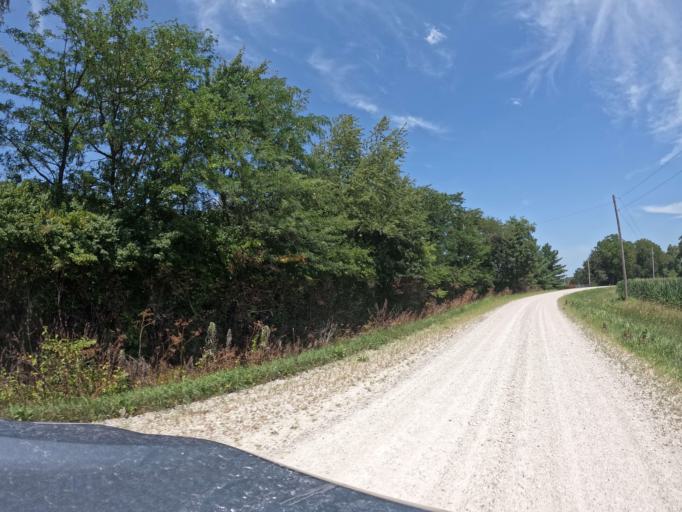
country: US
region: Iowa
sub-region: Henry County
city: Mount Pleasant
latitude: 40.9151
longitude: -91.5502
